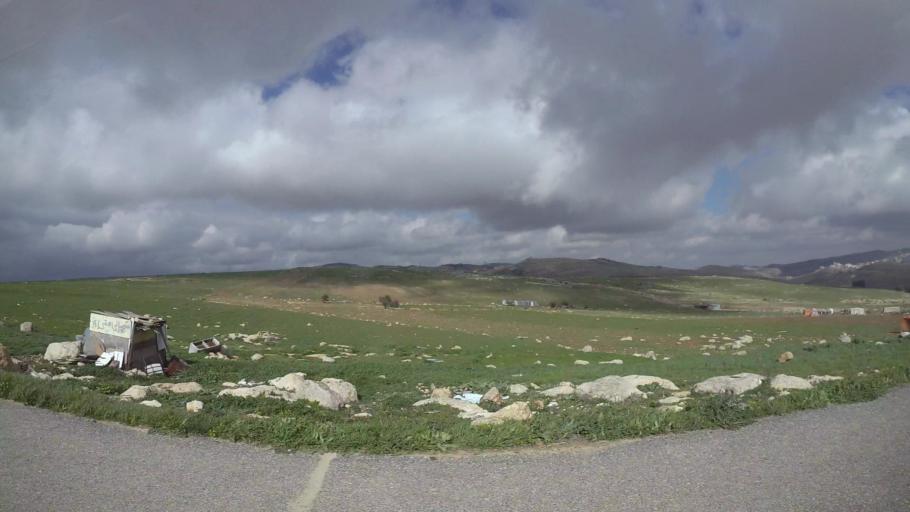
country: JO
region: Amman
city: Al Jubayhah
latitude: 32.0774
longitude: 35.8860
